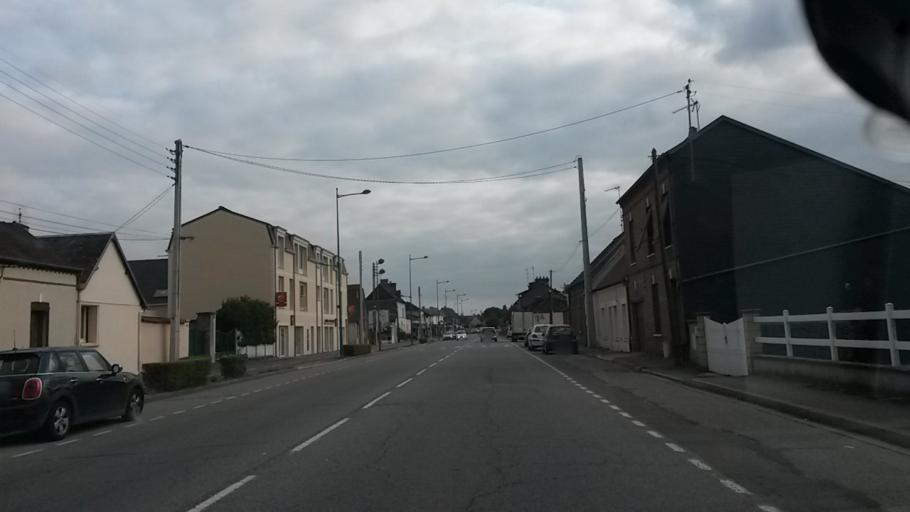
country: FR
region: Haute-Normandie
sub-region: Departement de l'Eure
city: Gravigny
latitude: 49.0493
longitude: 1.1639
